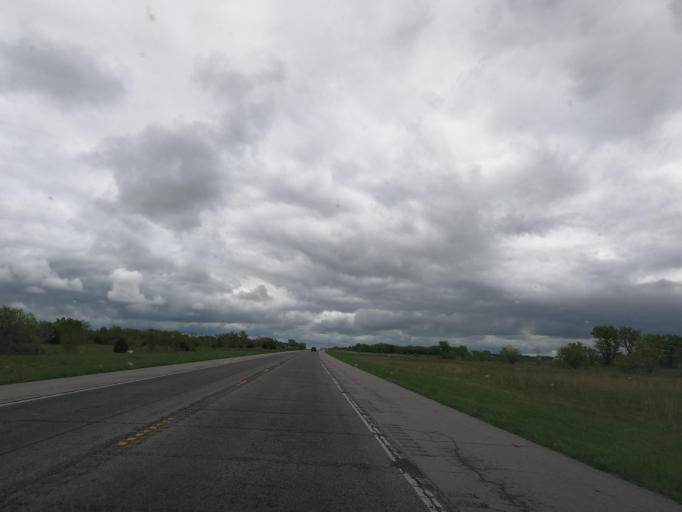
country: US
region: Kansas
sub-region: Montgomery County
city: Cherryvale
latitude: 37.3435
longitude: -95.4234
